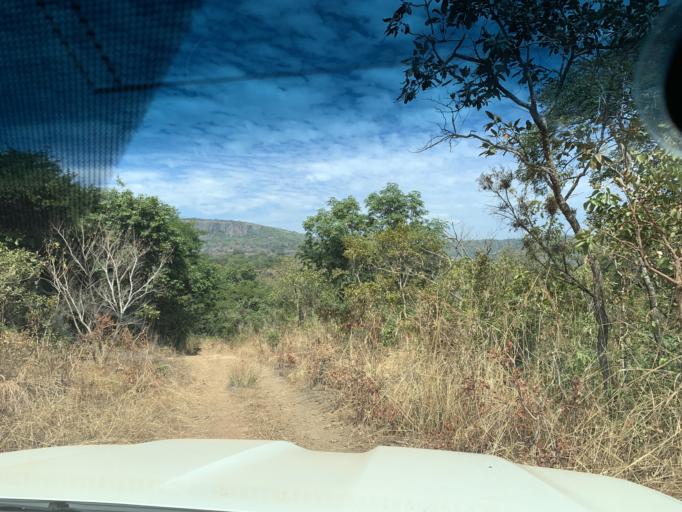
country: GN
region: Mamou
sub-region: Pita
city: Pita
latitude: 10.9945
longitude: -12.4891
